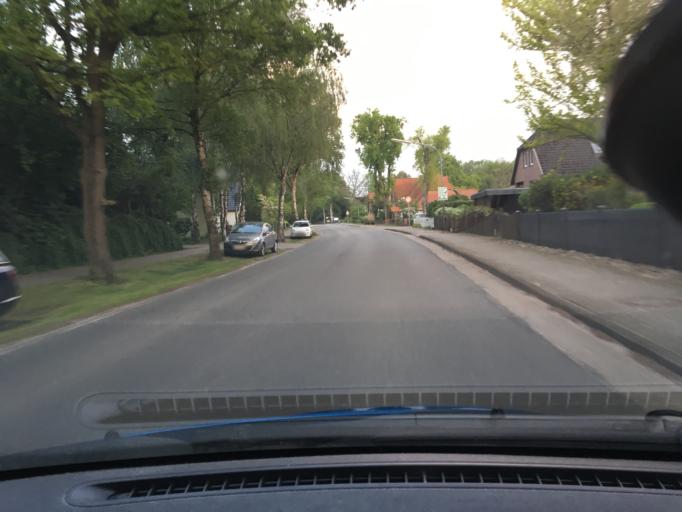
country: DE
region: Lower Saxony
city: Vierhofen
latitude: 53.2674
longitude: 10.2162
